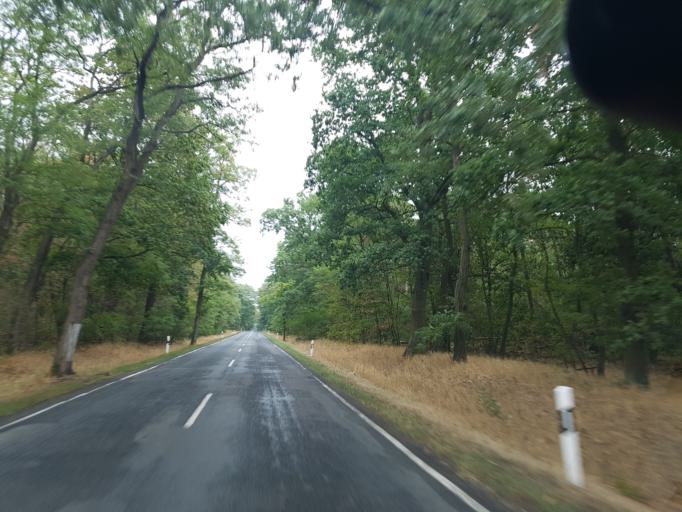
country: DE
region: Saxony-Anhalt
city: Loburg
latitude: 52.2266
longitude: 12.0818
